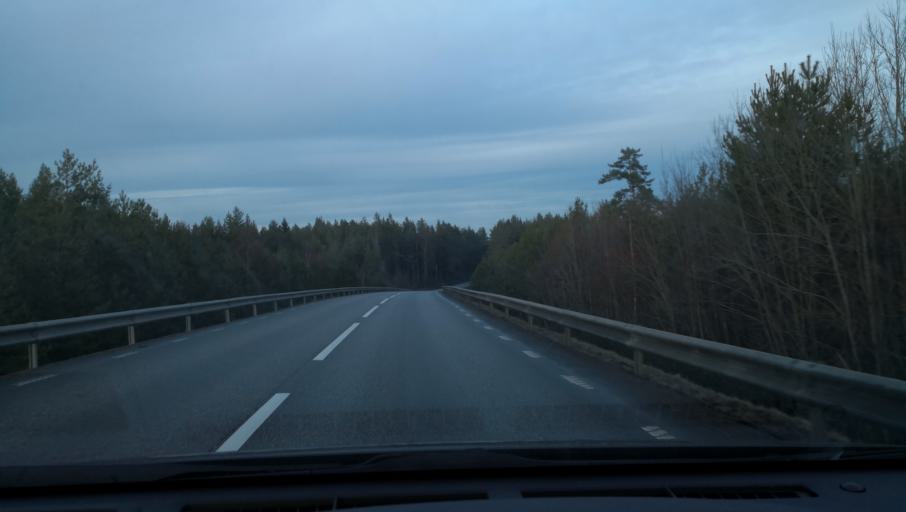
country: SE
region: OErebro
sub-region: Laxa Kommun
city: Laxa
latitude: 59.1215
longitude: 14.5847
